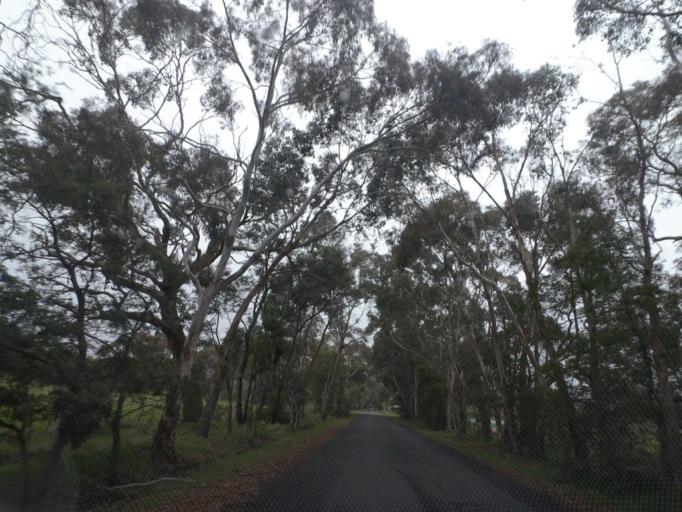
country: AU
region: Victoria
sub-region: Hume
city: Sunbury
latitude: -37.3343
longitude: 144.6048
